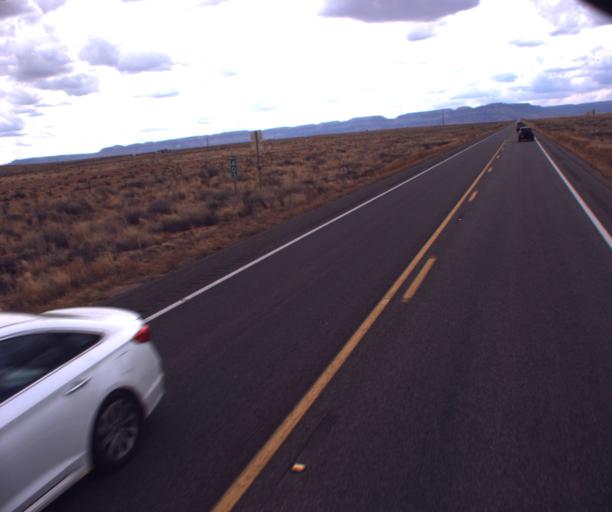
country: US
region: Arizona
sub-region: Navajo County
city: Kayenta
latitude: 36.7400
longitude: -110.0826
